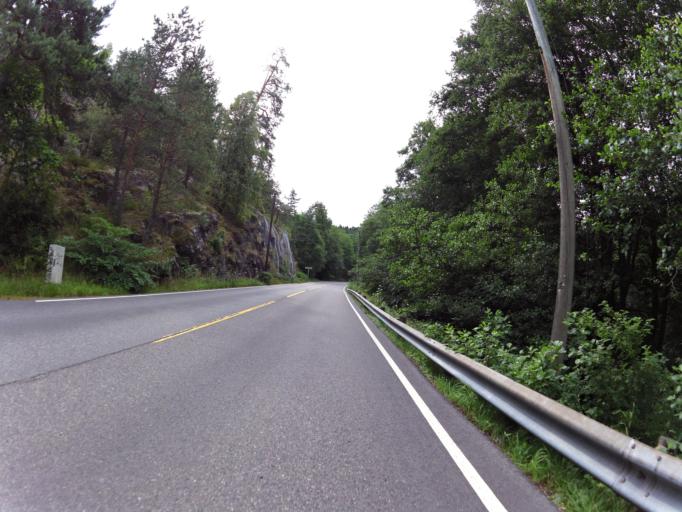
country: NO
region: Akershus
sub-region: Oppegard
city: Kolbotn
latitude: 59.8252
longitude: 10.7710
